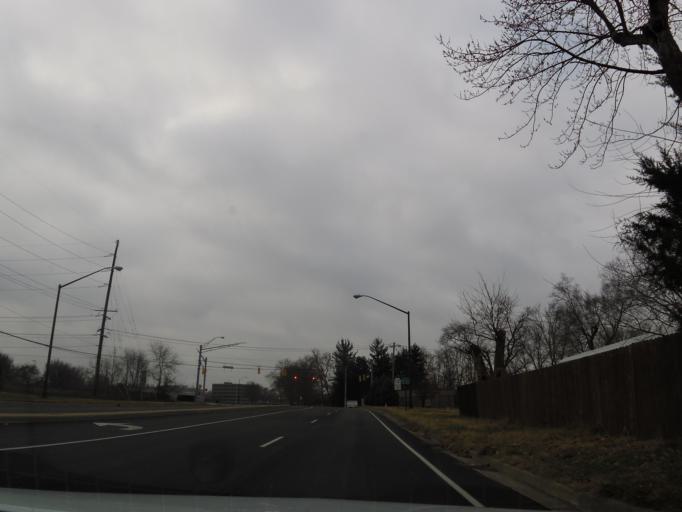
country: US
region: Indiana
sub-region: Bartholomew County
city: Columbus
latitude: 39.2070
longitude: -85.9042
